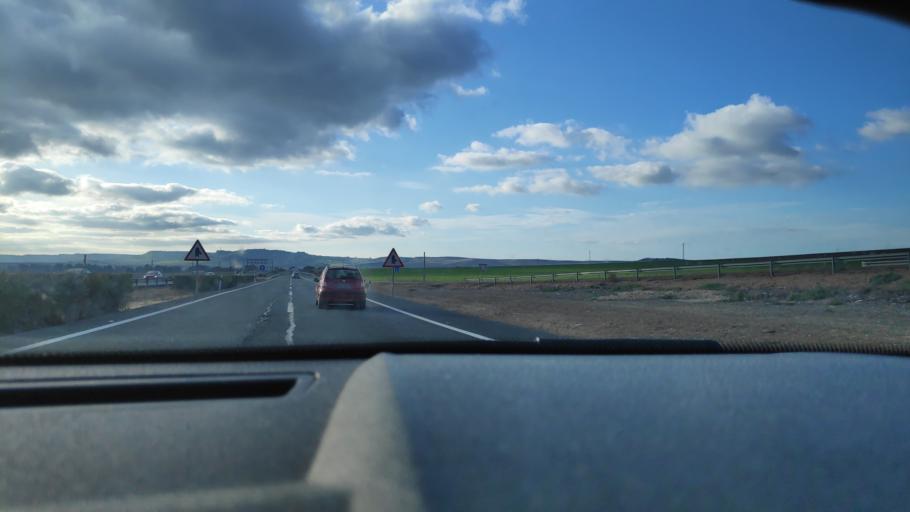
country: ES
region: Andalusia
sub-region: Provincia de Sevilla
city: Carmona
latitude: 37.4824
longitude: -5.5524
